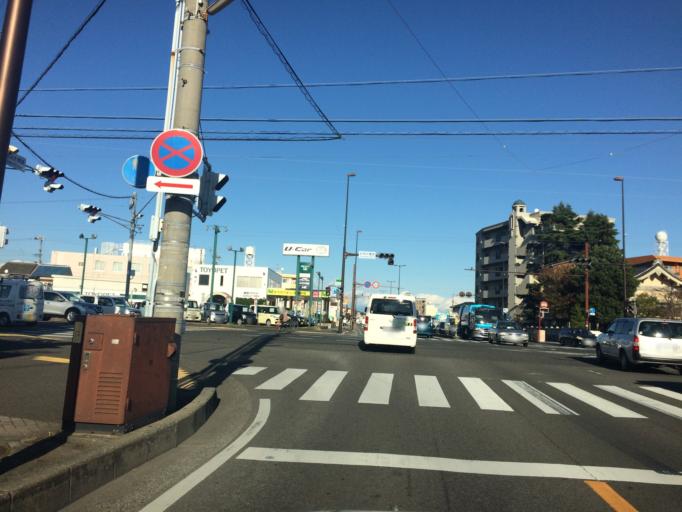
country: JP
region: Shizuoka
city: Shizuoka-shi
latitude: 34.9547
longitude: 138.3824
